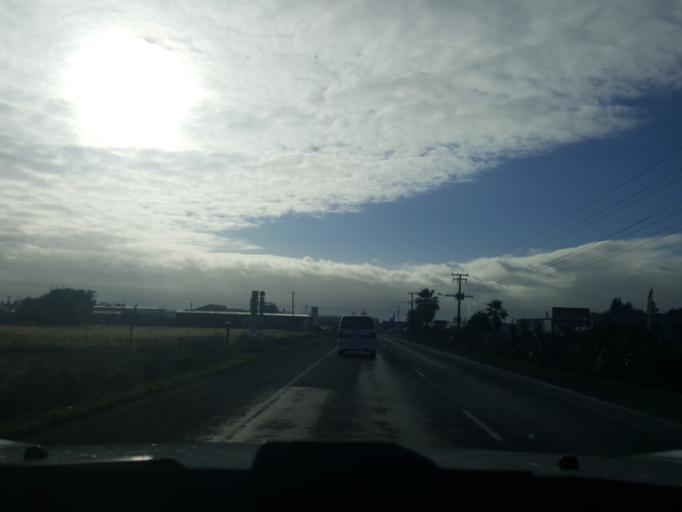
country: NZ
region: Waikato
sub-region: Waipa District
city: Cambridge
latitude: -37.6627
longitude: 175.5146
